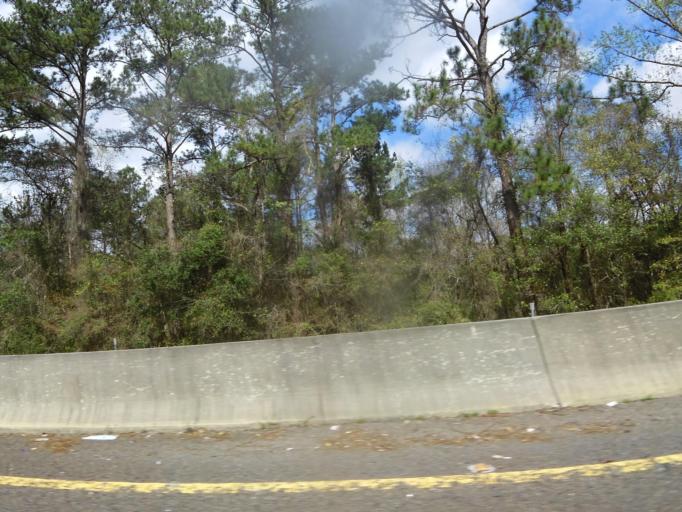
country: US
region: Florida
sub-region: Duval County
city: Baldwin
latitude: 30.3107
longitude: -81.8507
